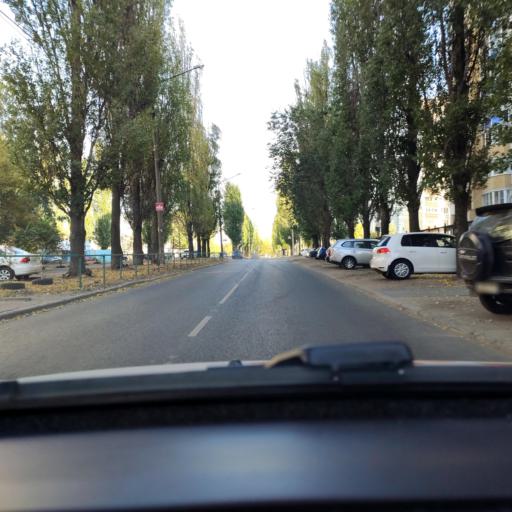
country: RU
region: Voronezj
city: Podgornoye
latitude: 51.6970
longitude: 39.1330
